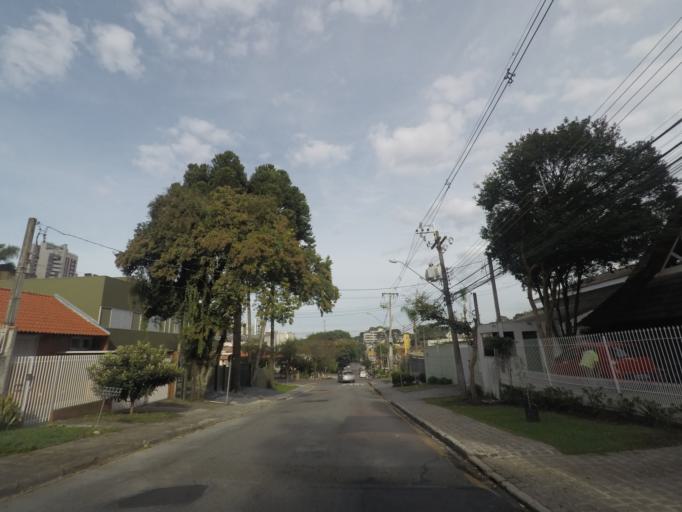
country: BR
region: Parana
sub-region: Curitiba
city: Curitiba
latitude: -25.4286
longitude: -49.2964
